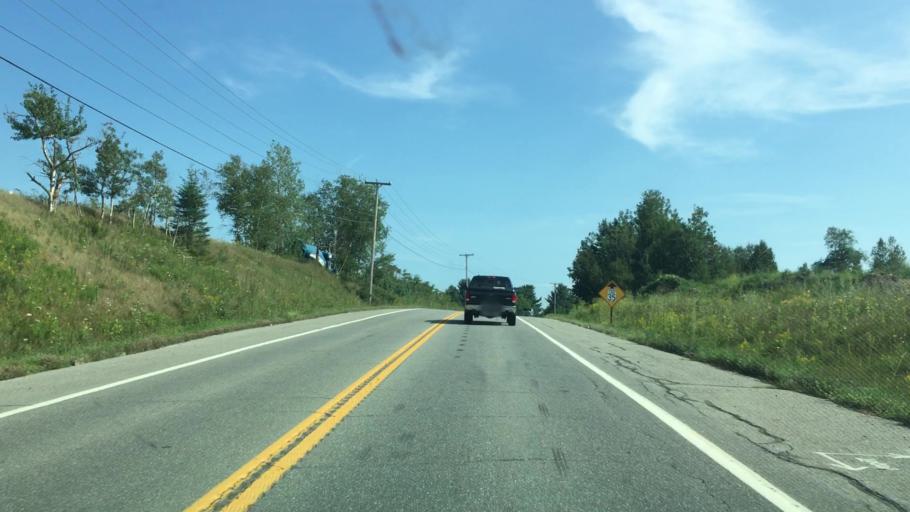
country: US
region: Maine
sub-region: Waldo County
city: Frankfort
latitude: 44.5572
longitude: -68.8654
